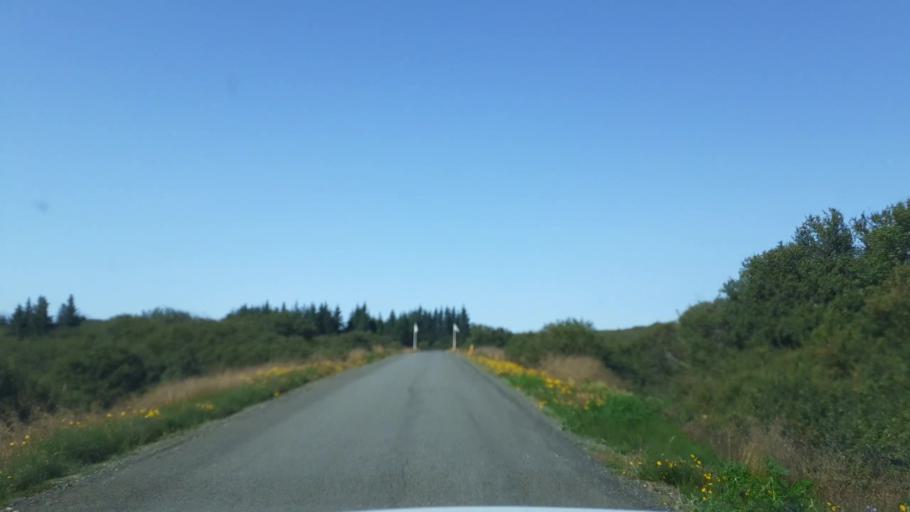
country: IS
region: West
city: Borgarnes
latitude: 64.7014
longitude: -21.6259
